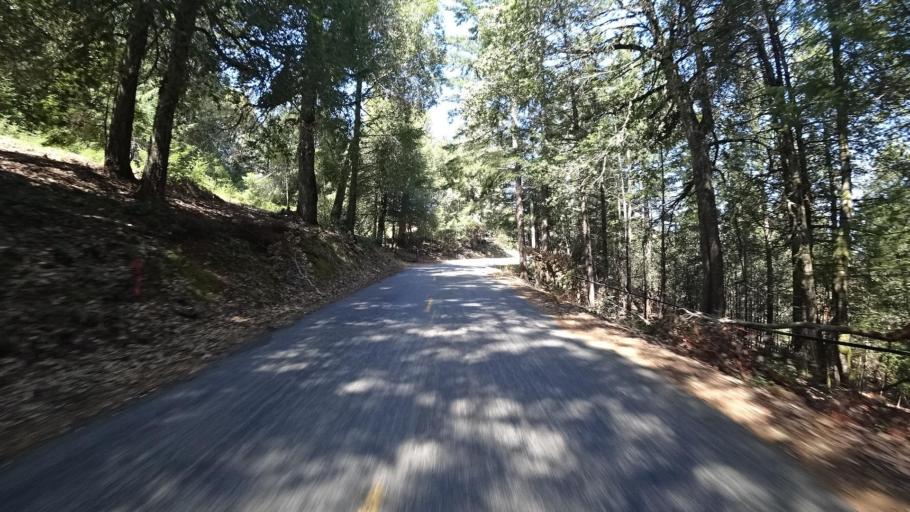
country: US
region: California
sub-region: Humboldt County
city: Redway
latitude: 40.0941
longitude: -123.6786
